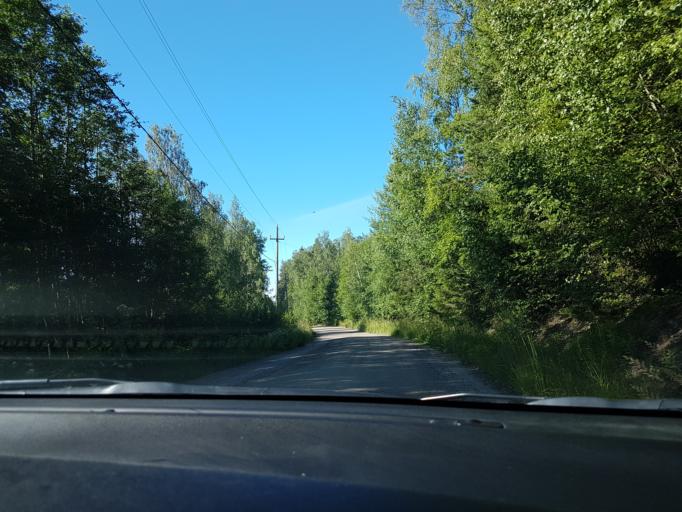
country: FI
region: Uusimaa
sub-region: Helsinki
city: Sibbo
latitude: 60.2848
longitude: 25.2398
